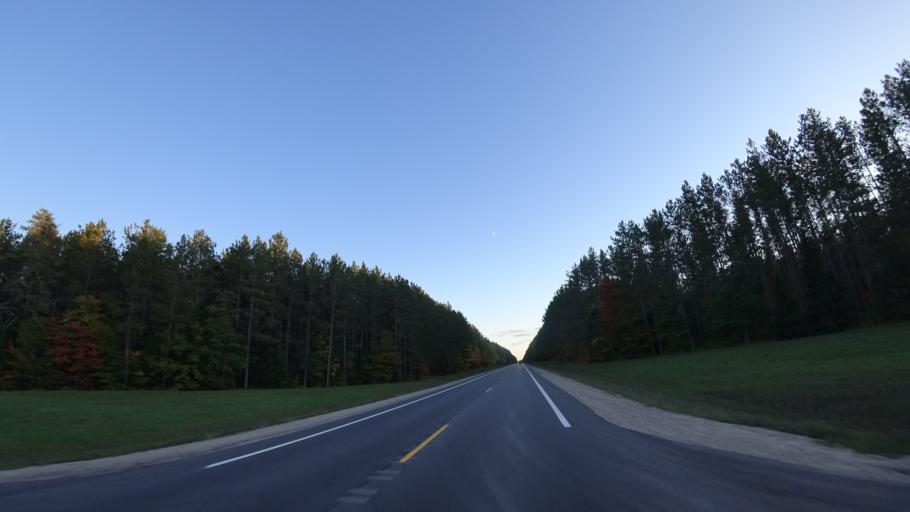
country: US
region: Michigan
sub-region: Luce County
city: Newberry
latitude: 46.3035
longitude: -85.0095
